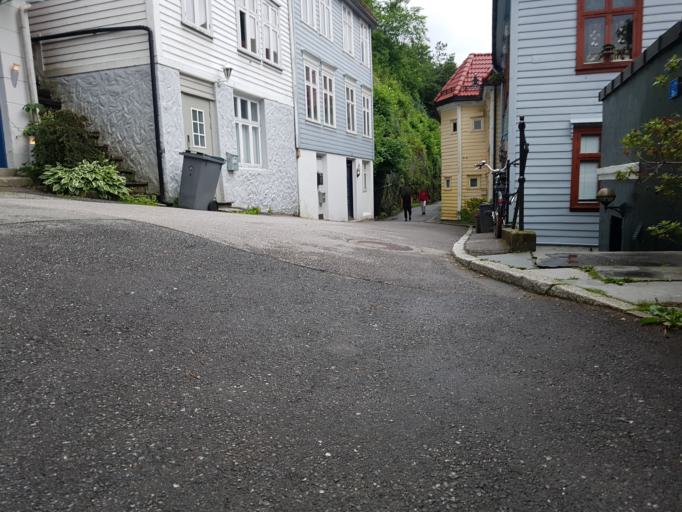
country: NO
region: Hordaland
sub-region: Bergen
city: Bergen
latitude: 60.3955
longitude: 5.3307
